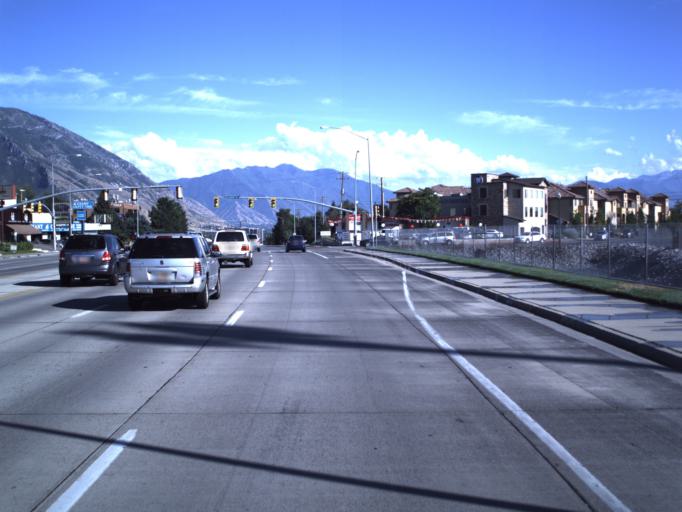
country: US
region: Utah
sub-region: Utah County
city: Orem
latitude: 40.2656
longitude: -111.6810
